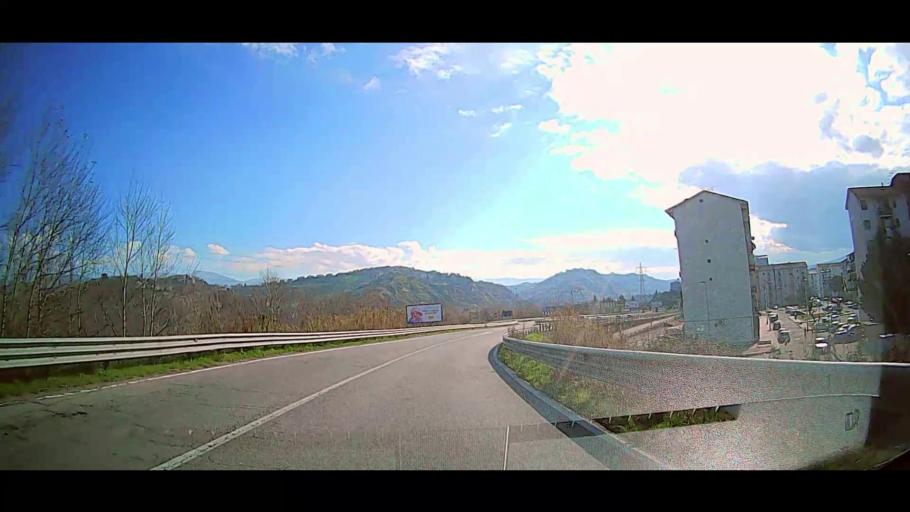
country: IT
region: Calabria
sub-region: Provincia di Cosenza
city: Quattromiglia
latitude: 39.3277
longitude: 16.2538
